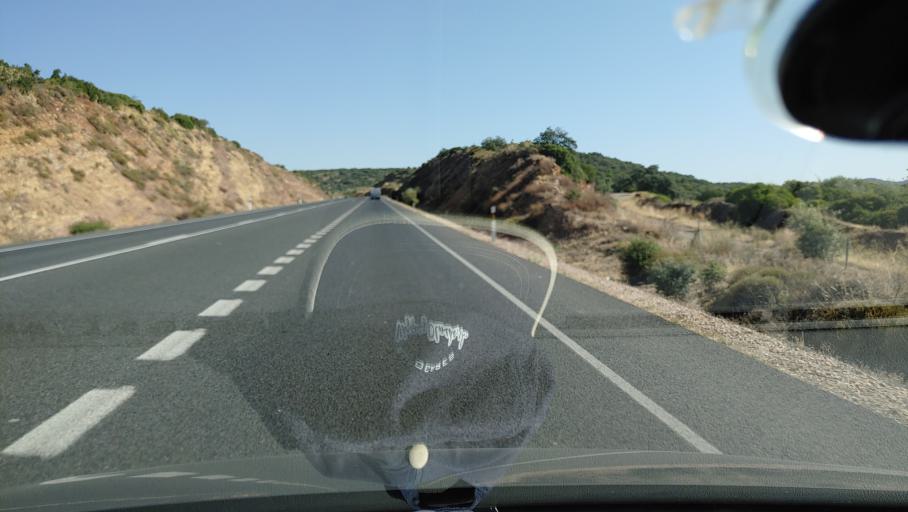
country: ES
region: Andalusia
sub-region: Province of Cordoba
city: Cordoba
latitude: 37.9353
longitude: -4.7639
